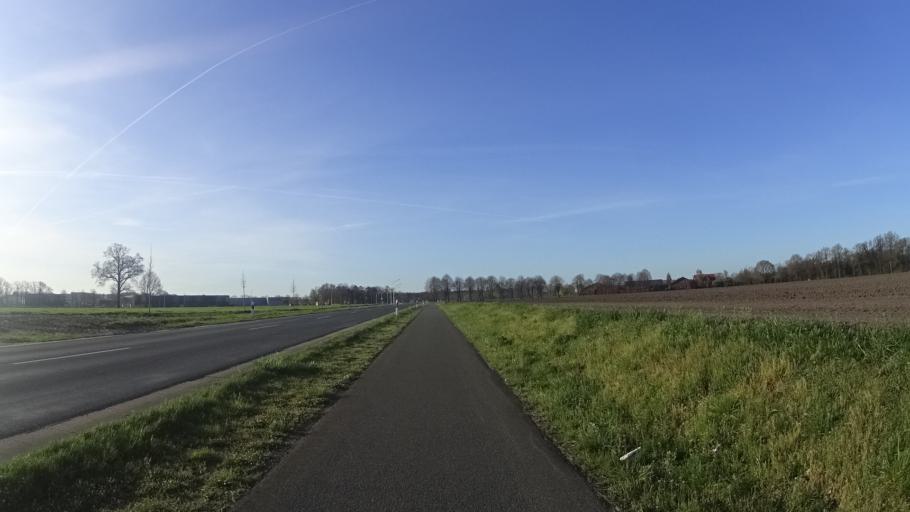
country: DE
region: North Rhine-Westphalia
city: Emsdetten
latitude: 52.1467
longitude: 7.5349
